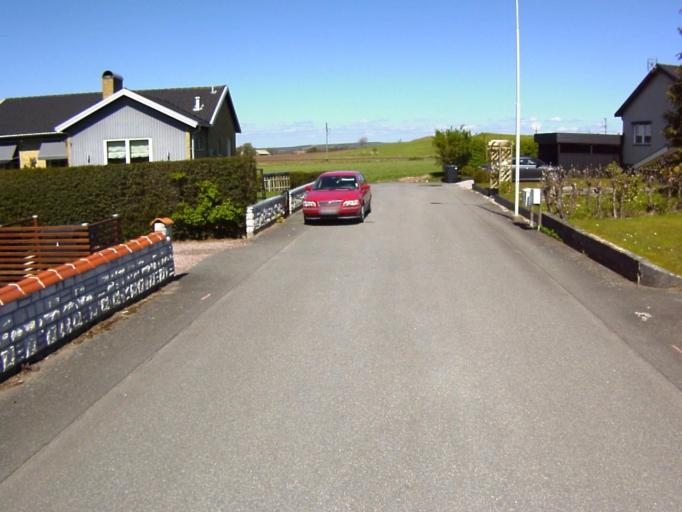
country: SE
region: Skane
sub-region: Kristianstads Kommun
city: Kristianstad
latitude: 56.0503
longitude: 14.2087
